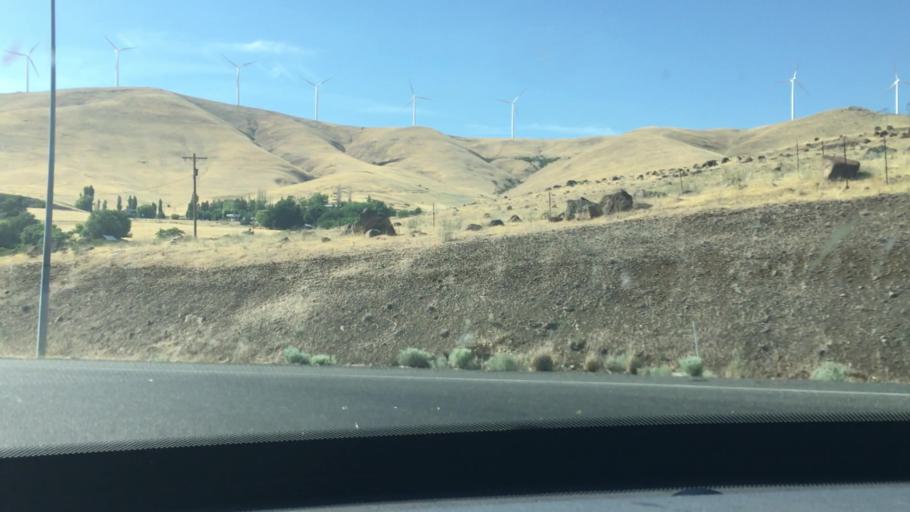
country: US
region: Washington
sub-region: Klickitat County
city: Goldendale
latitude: 45.6978
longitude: -120.8154
